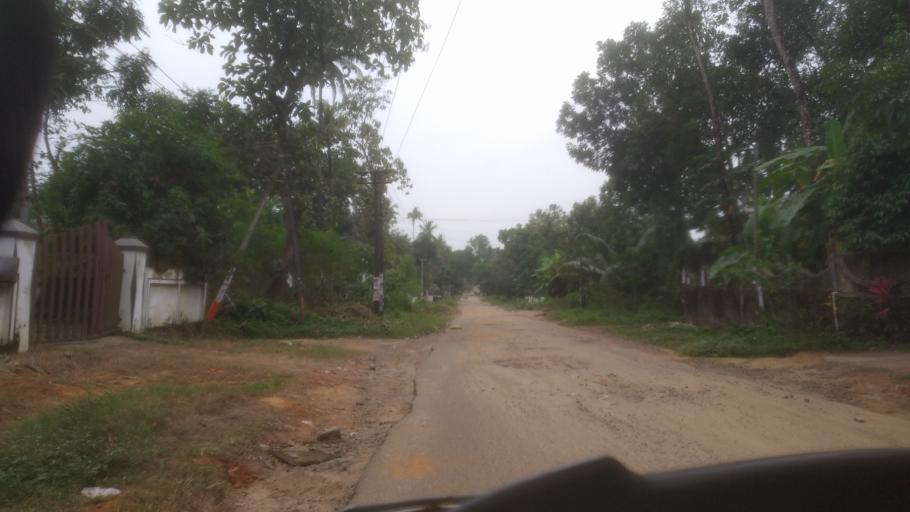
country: IN
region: Kerala
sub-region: Ernakulam
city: Perumbavoor
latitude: 10.0540
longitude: 76.5199
